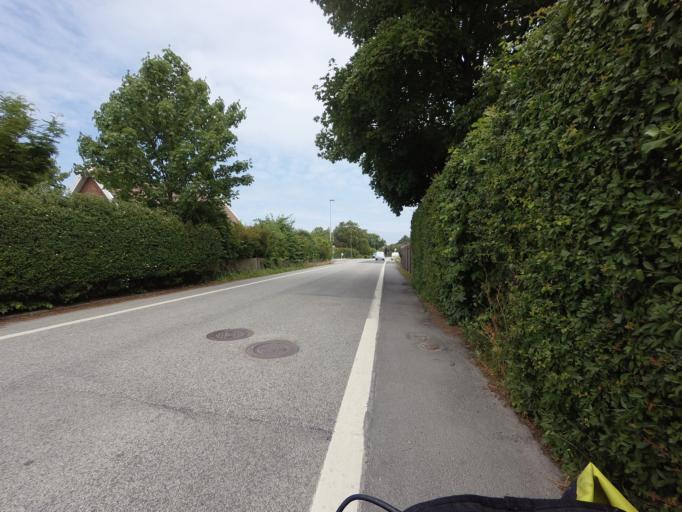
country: SE
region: Skane
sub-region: Malmo
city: Bunkeflostrand
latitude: 55.5341
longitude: 12.9223
